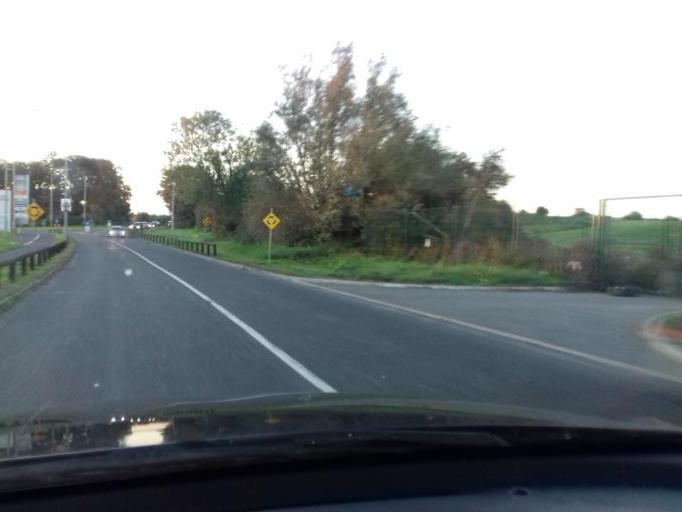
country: IE
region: Leinster
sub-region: Lu
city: Drogheda
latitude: 53.7267
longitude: -6.3836
